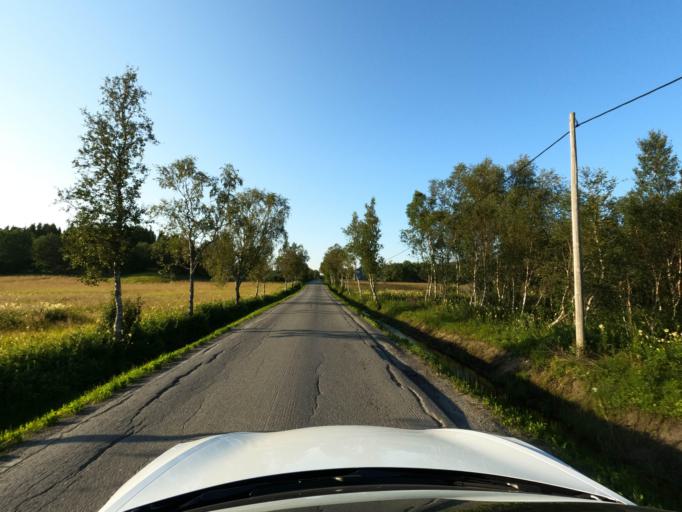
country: NO
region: Troms
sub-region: Skanland
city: Evenskjer
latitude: 68.4677
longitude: 16.7018
